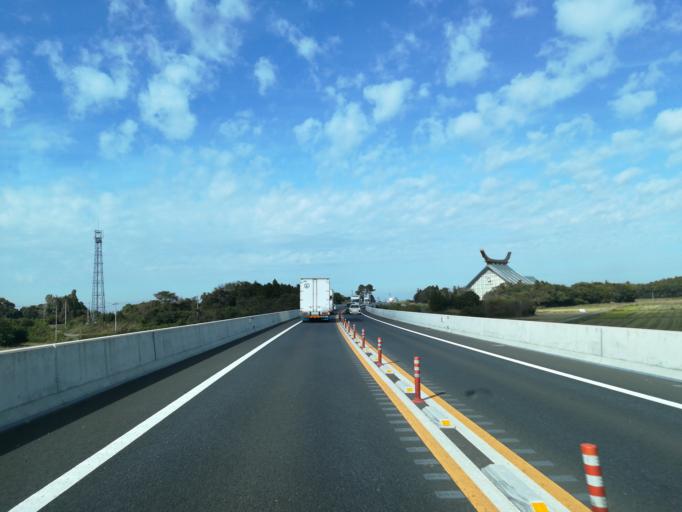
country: JP
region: Ibaraki
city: Mitsukaido
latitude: 36.0716
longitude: 140.0157
